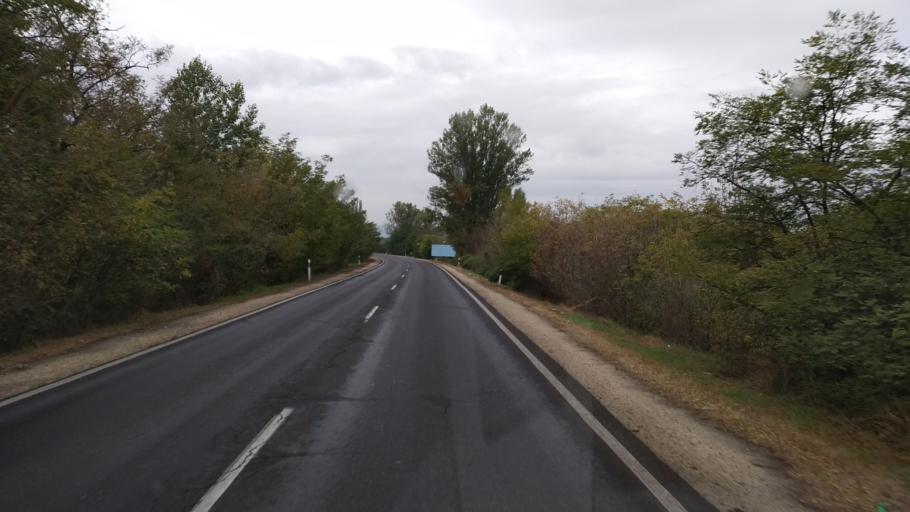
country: HU
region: Pest
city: Dunakeszi
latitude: 47.6216
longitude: 19.1160
